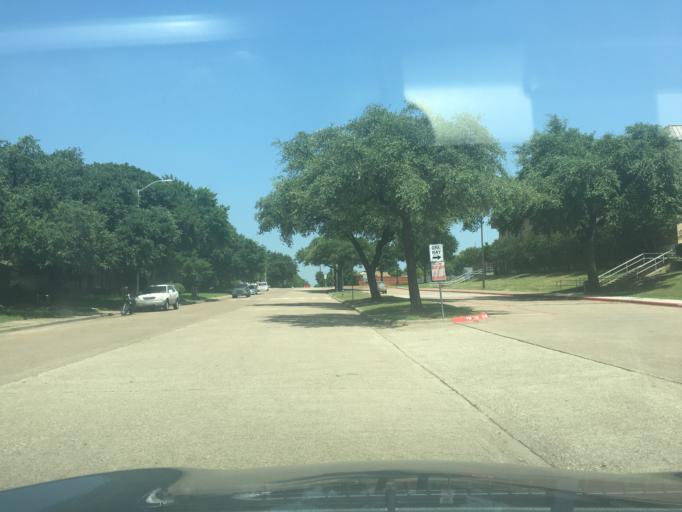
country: US
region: Texas
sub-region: Dallas County
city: Richardson
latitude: 32.9241
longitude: -96.7074
